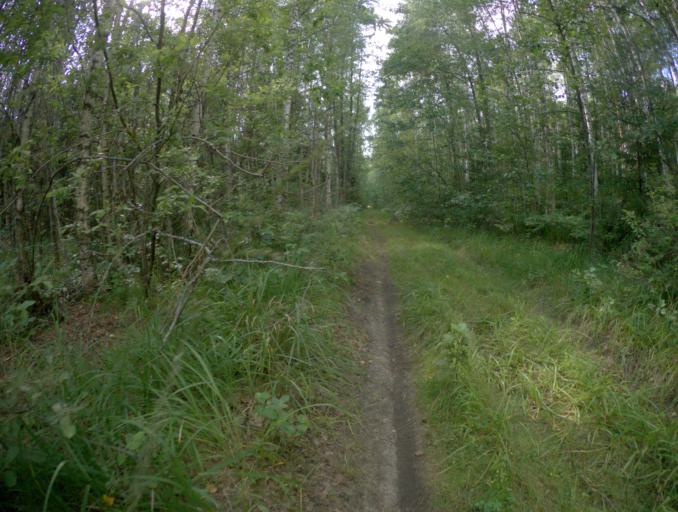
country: RU
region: Vladimir
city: Sobinka
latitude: 55.9140
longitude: 40.1017
